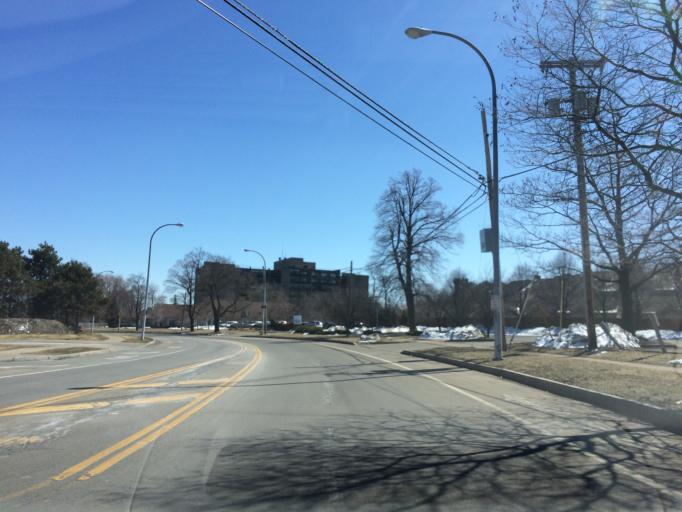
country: US
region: New York
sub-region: Monroe County
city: Brighton
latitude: 43.1496
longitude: -77.5648
